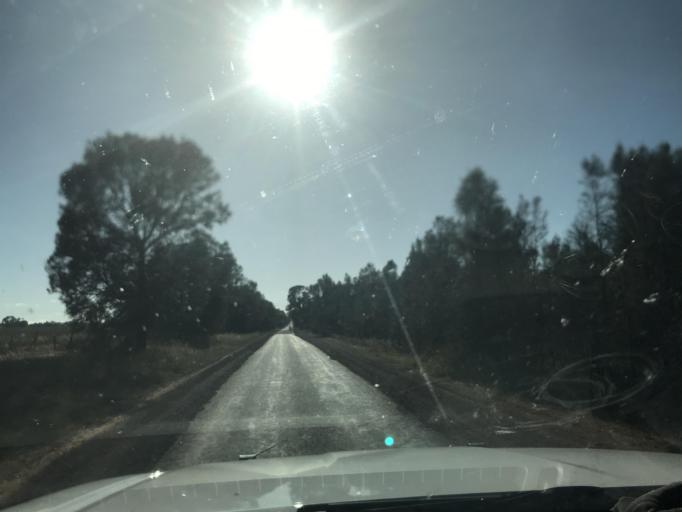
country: AU
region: Victoria
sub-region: Horsham
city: Horsham
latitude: -37.0050
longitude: 141.6202
